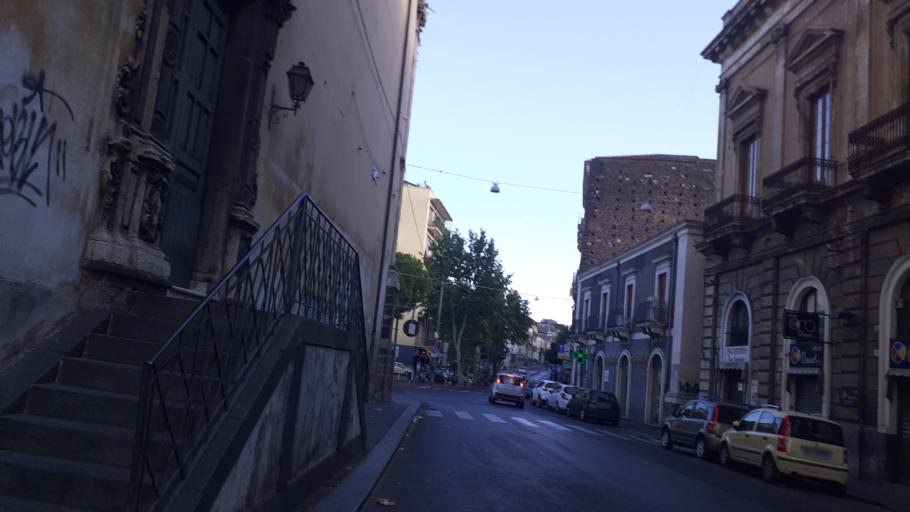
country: IT
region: Sicily
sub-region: Catania
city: Catania
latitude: 37.5083
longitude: 15.0829
